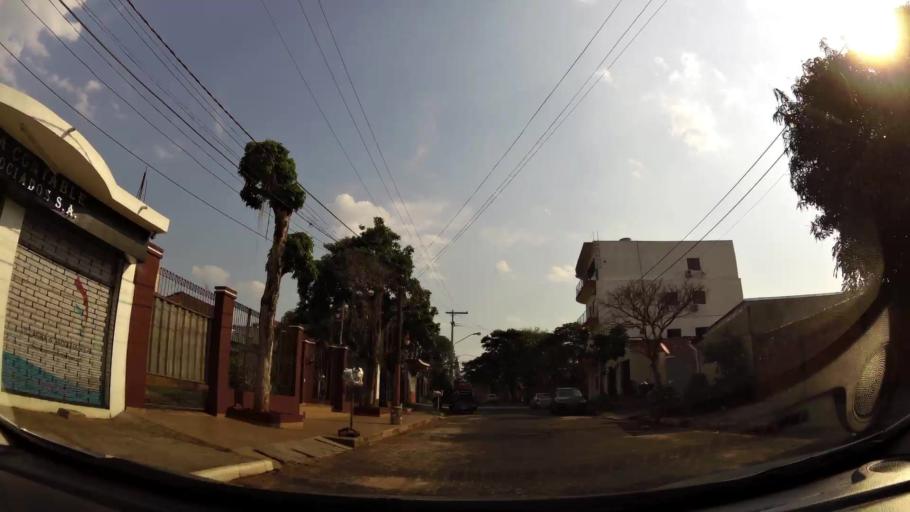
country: PY
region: Alto Parana
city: Presidente Franco
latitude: -25.5291
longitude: -54.6238
